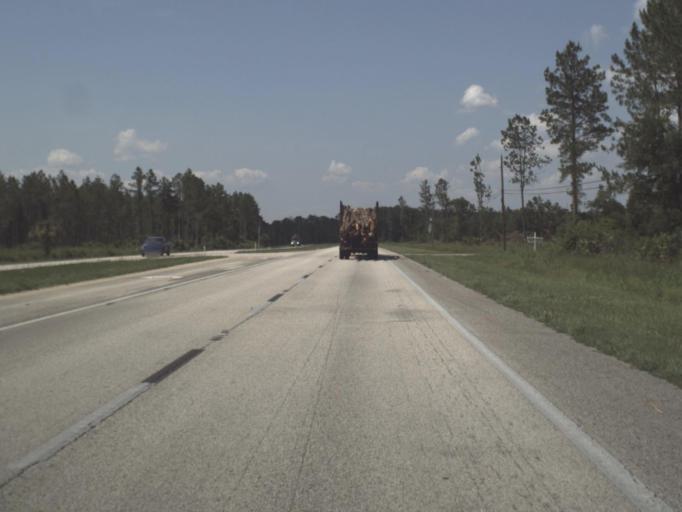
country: US
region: Florida
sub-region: Marion County
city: Citra
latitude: 29.4930
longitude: -82.1001
